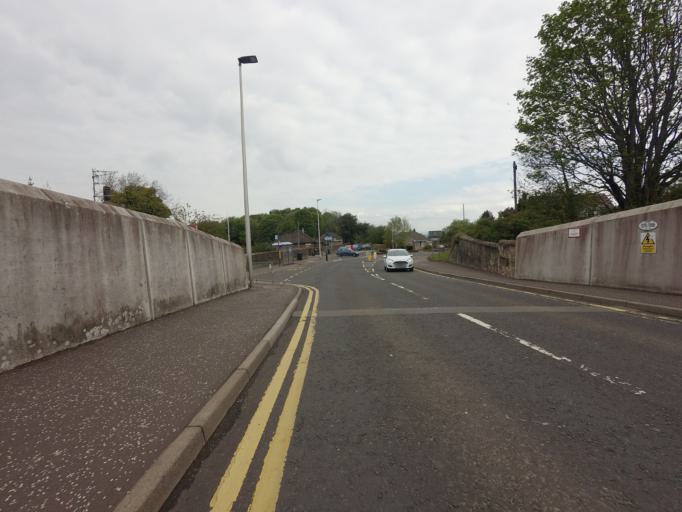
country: GB
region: Scotland
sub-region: Falkirk
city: Polmont
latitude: 55.9846
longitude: -3.7147
